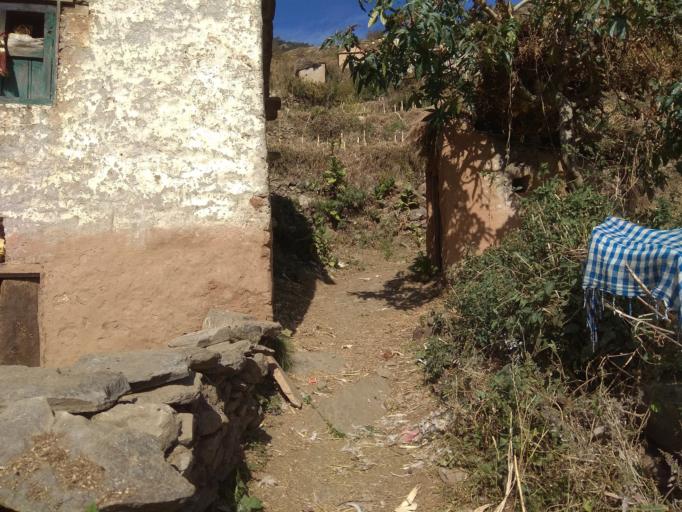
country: NP
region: Mid Western
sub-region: Bheri Zone
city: Dailekh
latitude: 29.2961
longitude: 81.7180
